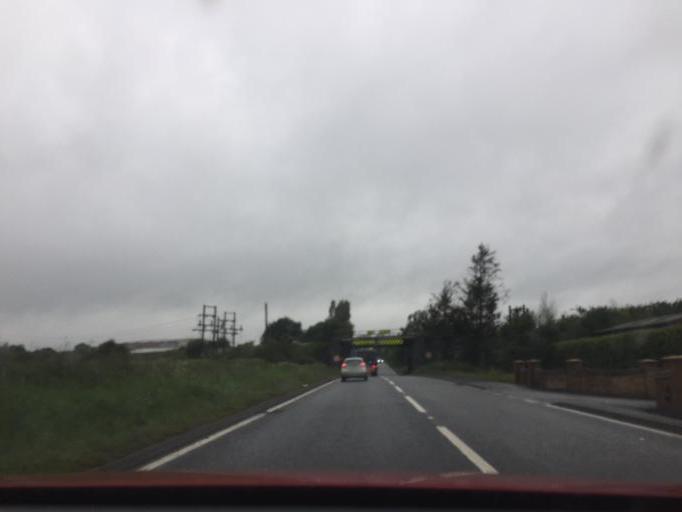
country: GB
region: England
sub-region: Leicestershire
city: Hinckley
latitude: 52.5301
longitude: -1.4014
